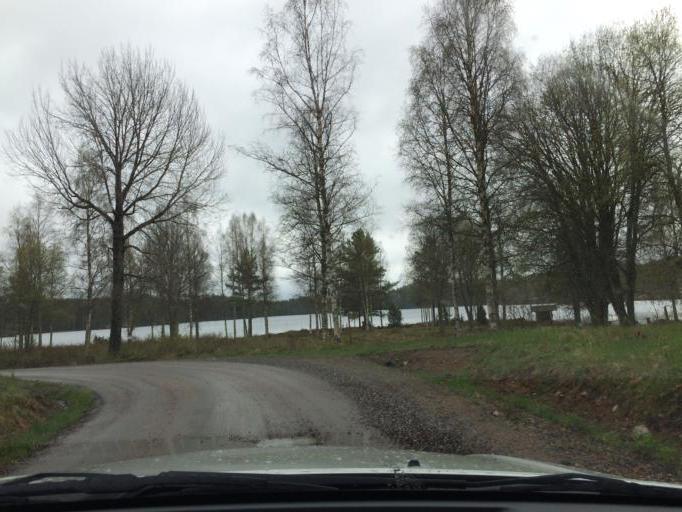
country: SE
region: Dalarna
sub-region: Ludvika Kommun
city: Abborrberget
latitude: 60.0222
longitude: 14.6261
